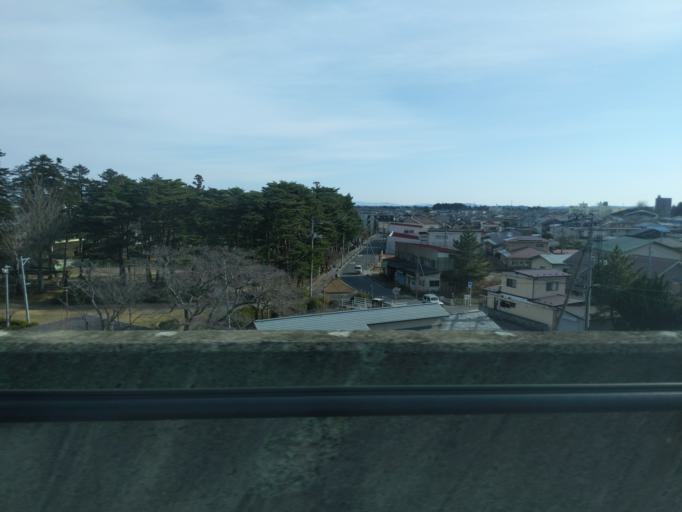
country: JP
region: Miyagi
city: Furukawa
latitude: 38.5807
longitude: 140.9705
